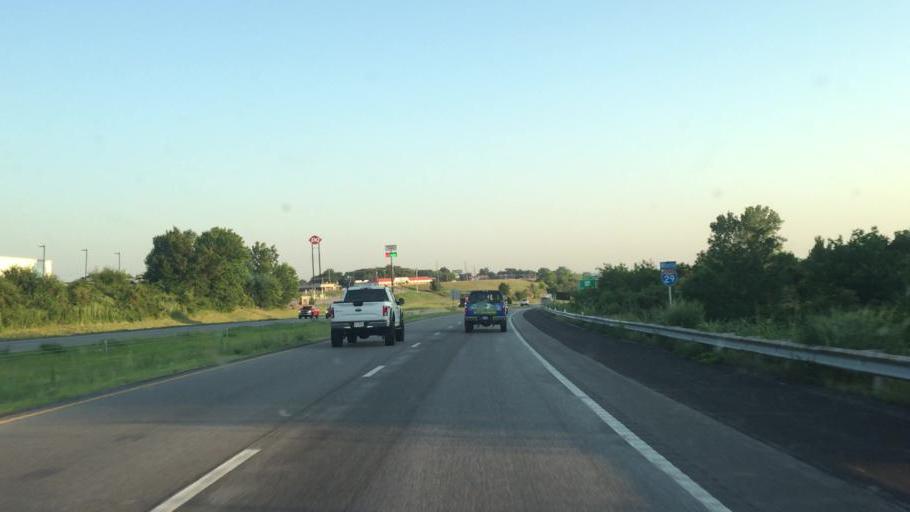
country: US
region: Missouri
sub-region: Platte County
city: Platte City
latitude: 39.3580
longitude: -94.7664
